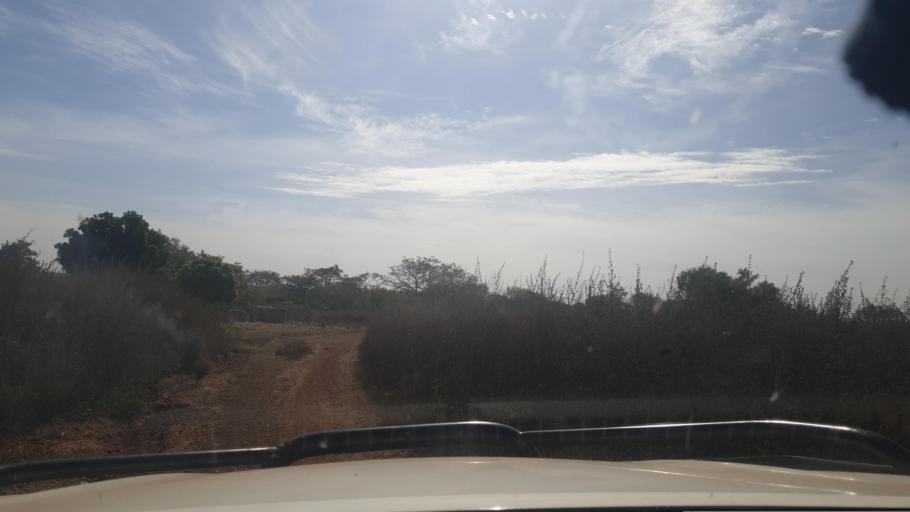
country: GN
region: Kankan
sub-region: Mandiana Prefecture
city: Mandiana
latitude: 10.4878
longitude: -8.0961
